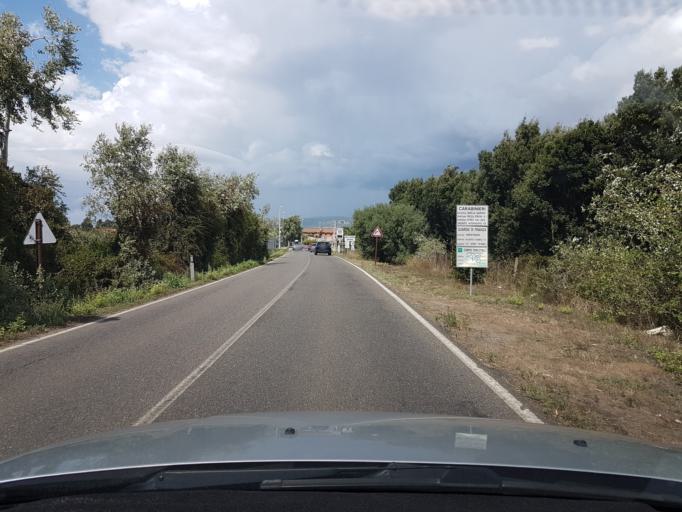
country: IT
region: Sardinia
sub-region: Provincia di Oristano
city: Riola Sardo
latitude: 39.9869
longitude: 8.5405
